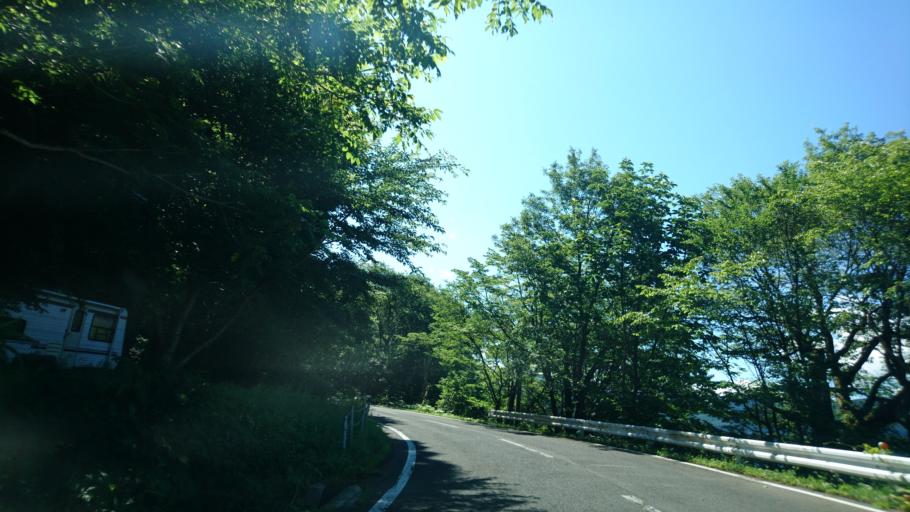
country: JP
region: Akita
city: Kakunodatemachi
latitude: 39.7472
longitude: 140.6791
